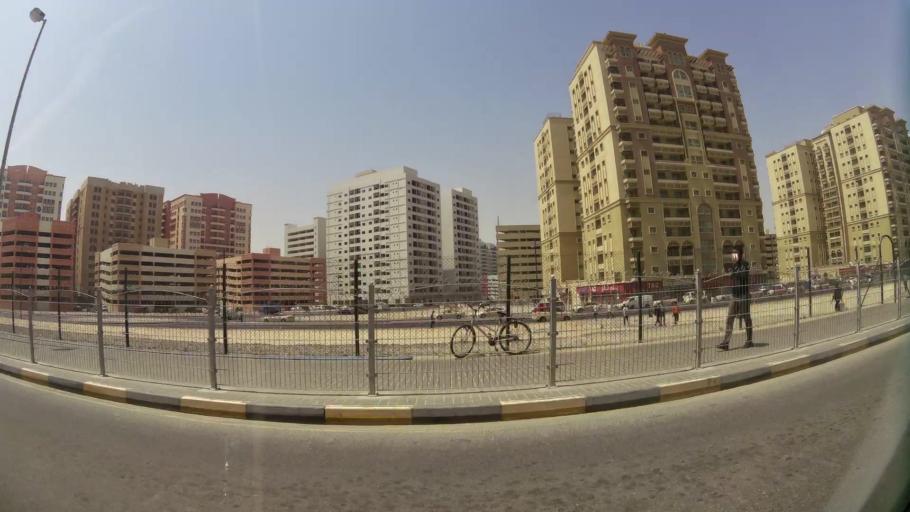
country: AE
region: Ash Shariqah
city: Sharjah
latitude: 25.2972
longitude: 55.3707
